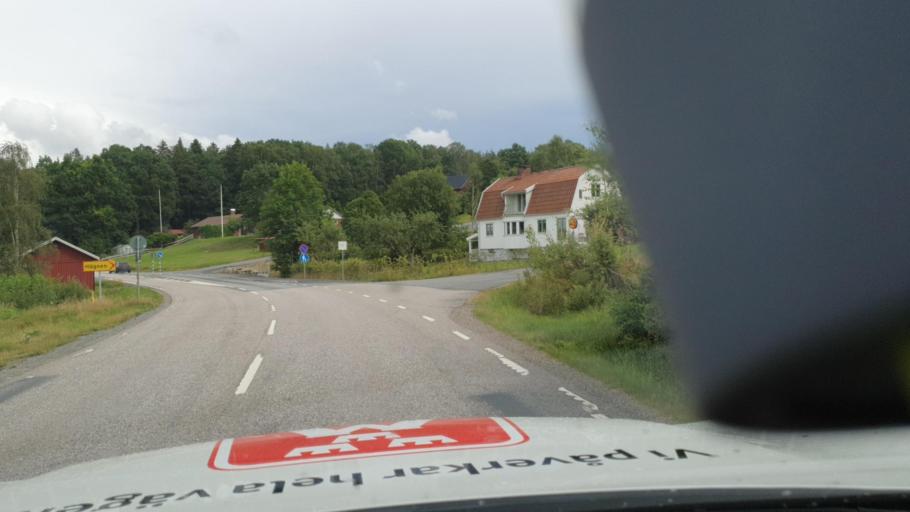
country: SE
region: Vaestra Goetaland
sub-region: Harryda Kommun
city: Hindas
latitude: 57.6100
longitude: 12.3824
